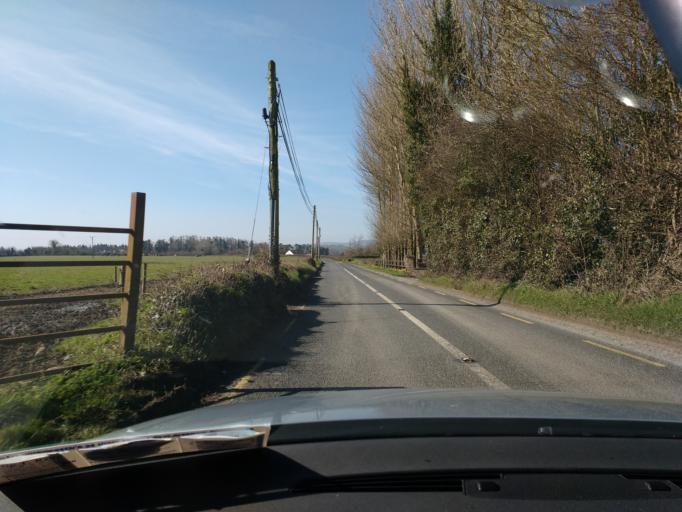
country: IE
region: Munster
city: Thurles
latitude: 52.6889
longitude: -7.8525
